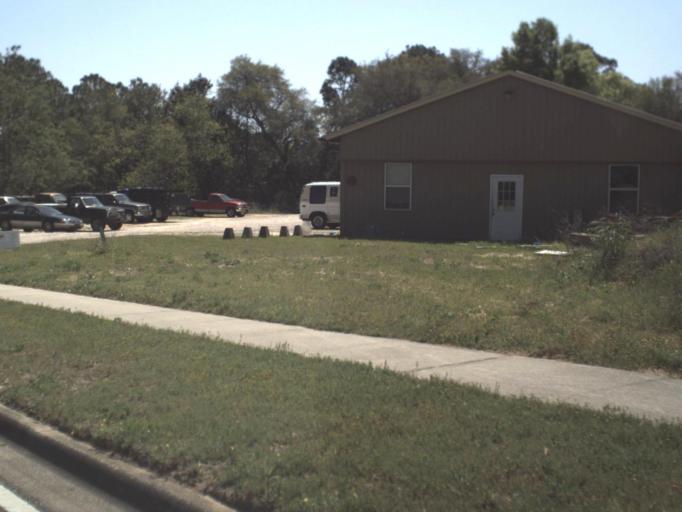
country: US
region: Florida
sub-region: Okaloosa County
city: Niceville
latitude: 30.5280
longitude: -86.4681
